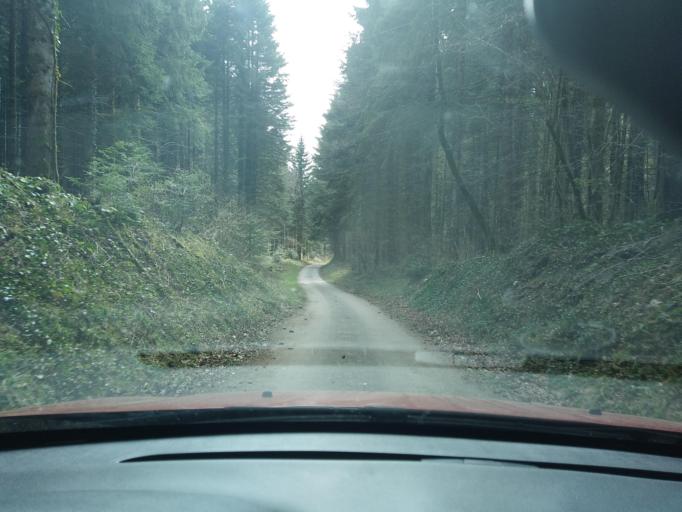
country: FR
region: Franche-Comte
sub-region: Departement du Jura
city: Moirans-en-Montagne
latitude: 46.4690
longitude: 5.7513
